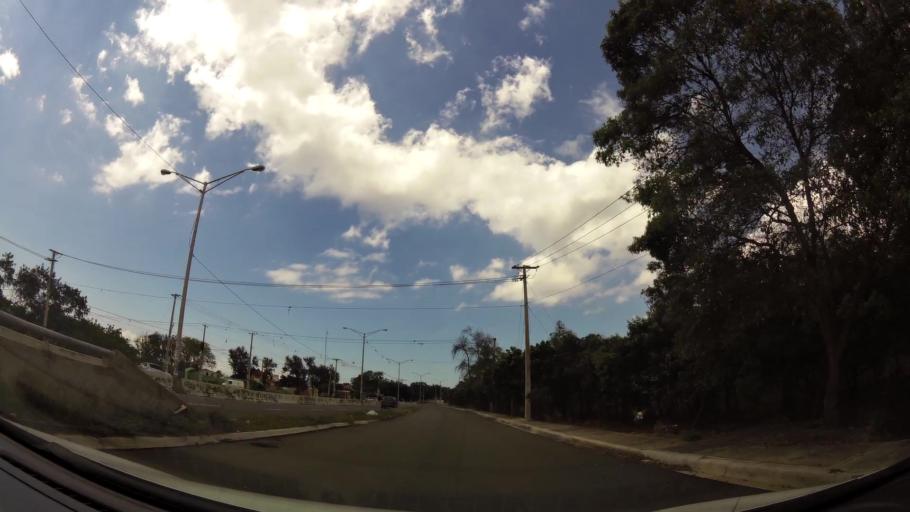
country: DO
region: Santo Domingo
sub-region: Santo Domingo
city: Santo Domingo Este
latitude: 18.4803
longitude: -69.8417
